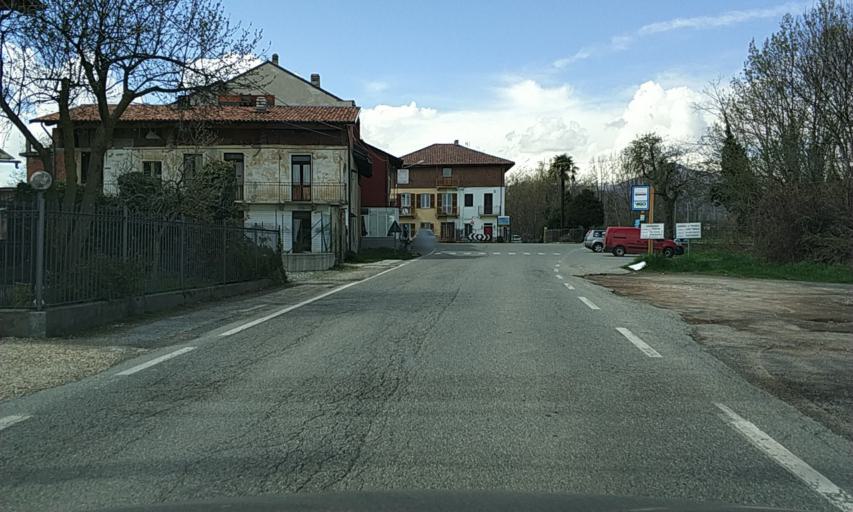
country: IT
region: Piedmont
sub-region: Provincia di Torino
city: Nole
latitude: 45.2574
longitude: 7.5826
